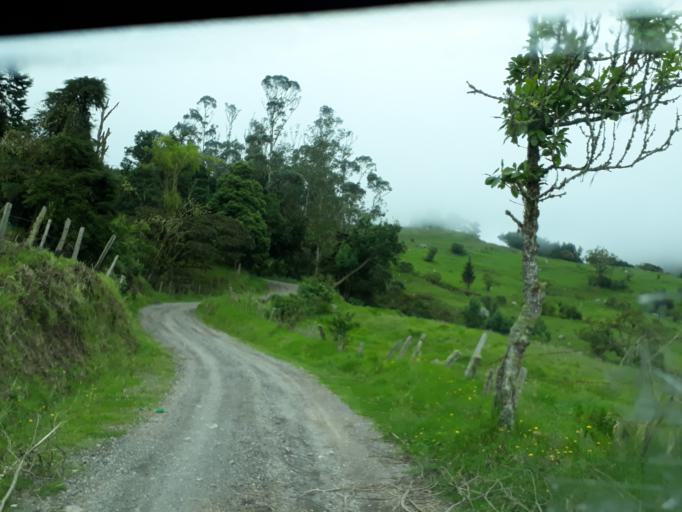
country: CO
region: Cundinamarca
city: Carmen de Carupa
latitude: 5.3744
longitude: -73.9754
